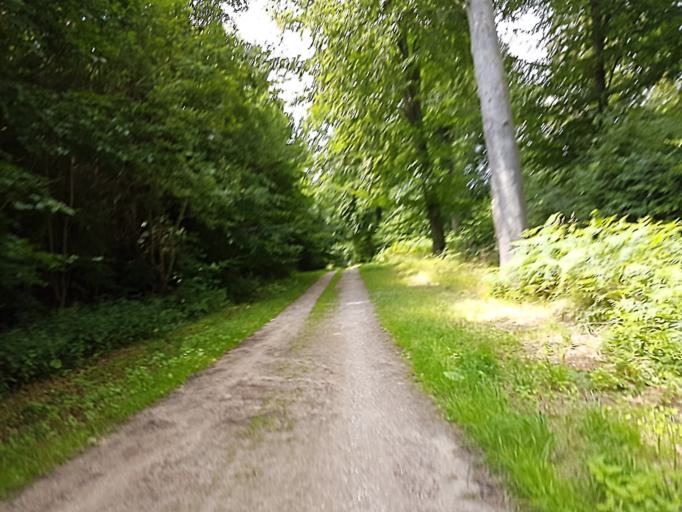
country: DK
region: Capital Region
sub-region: Fureso Kommune
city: Farum
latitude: 55.7965
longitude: 12.3520
